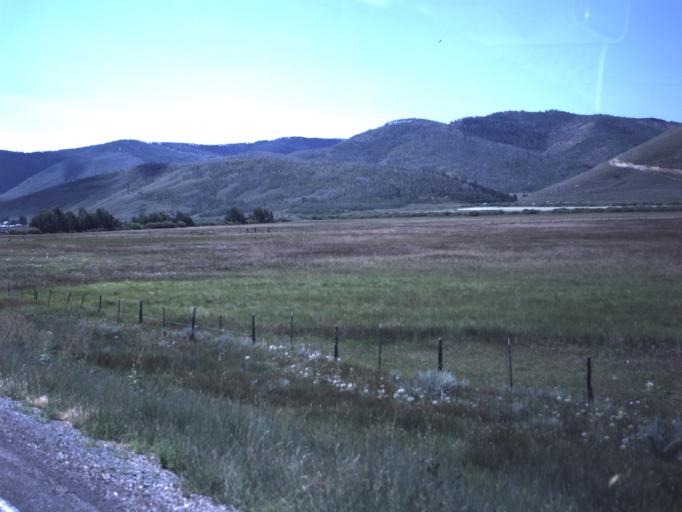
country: US
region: Utah
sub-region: Carbon County
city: Helper
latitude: 39.7436
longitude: -111.1514
